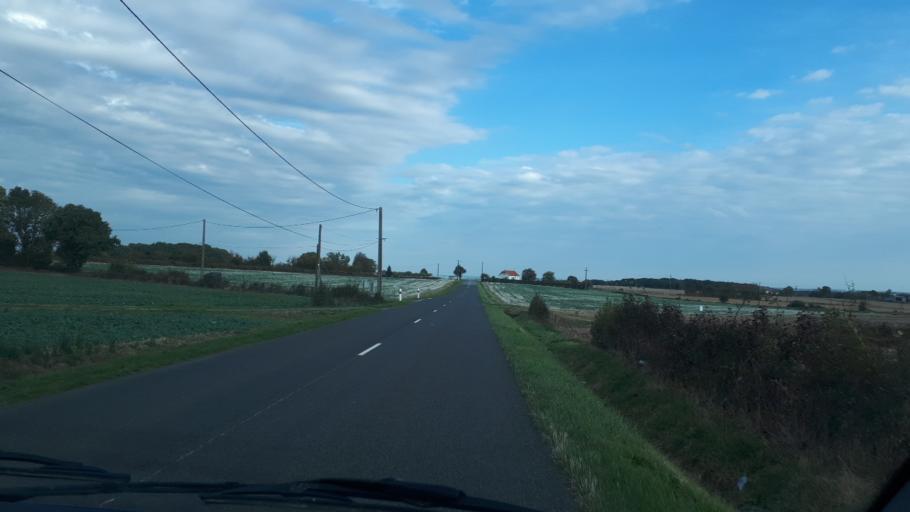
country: FR
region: Centre
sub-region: Departement du Loir-et-Cher
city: Mondoubleau
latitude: 47.9536
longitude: 0.9316
